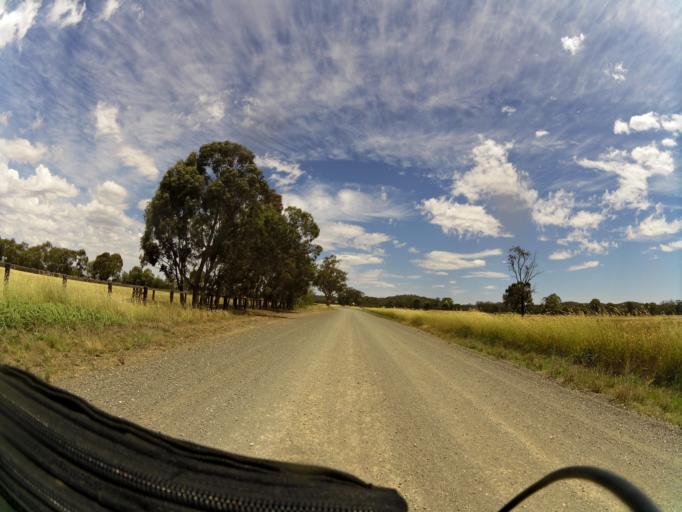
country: AU
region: Victoria
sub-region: Campaspe
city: Kyabram
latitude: -36.7576
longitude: 145.1023
